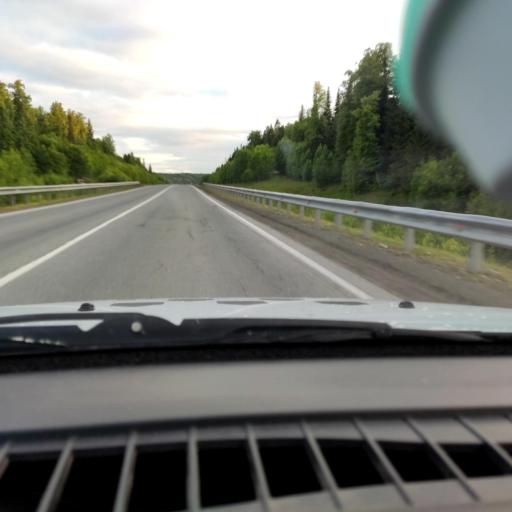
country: RU
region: Perm
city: Sylva
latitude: 58.2902
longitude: 56.7473
